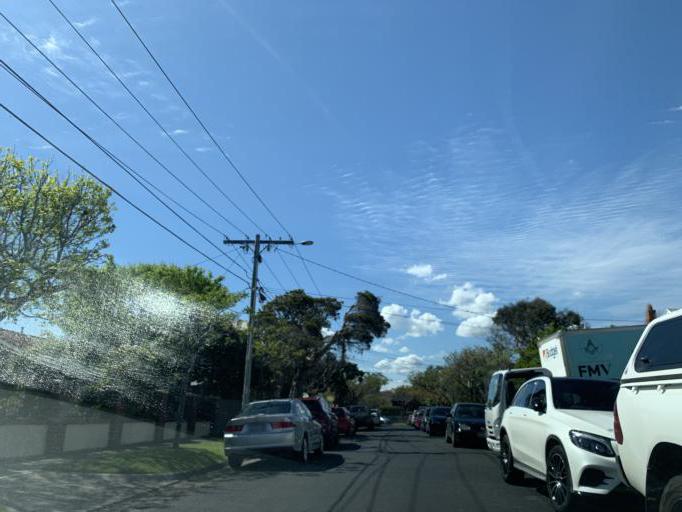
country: AU
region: Victoria
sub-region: Bayside
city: Black Rock
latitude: -37.9597
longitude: 145.0116
